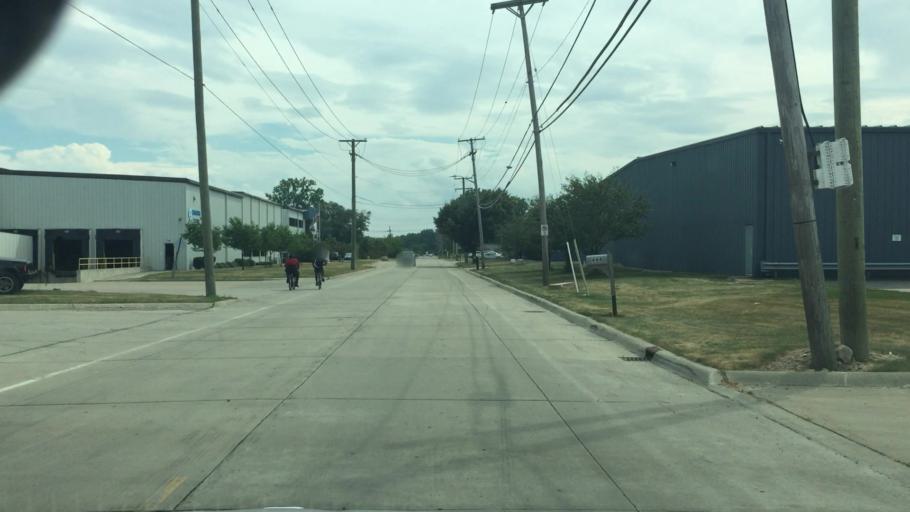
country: US
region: Michigan
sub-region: Monroe County
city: Monroe
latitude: 41.9168
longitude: -83.3715
